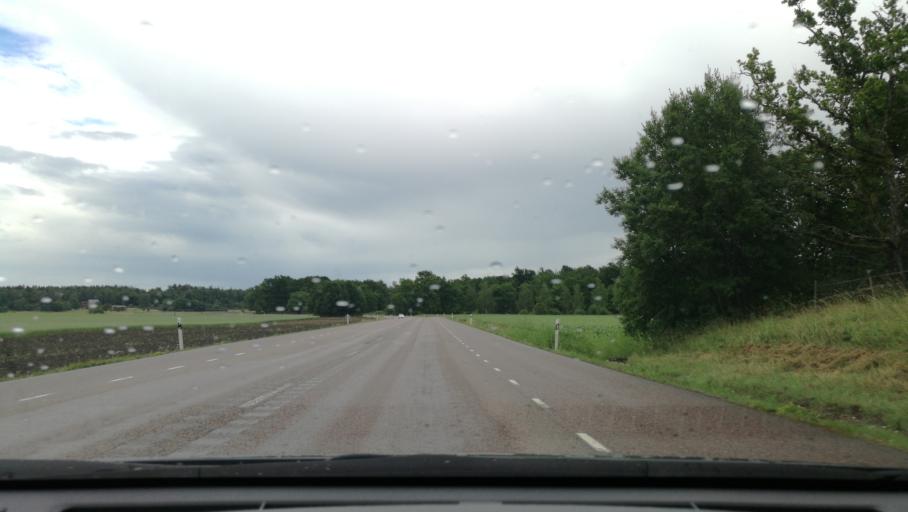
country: SE
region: Vaestmanland
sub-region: Kungsors Kommun
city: Kungsoer
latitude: 59.4347
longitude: 16.0649
